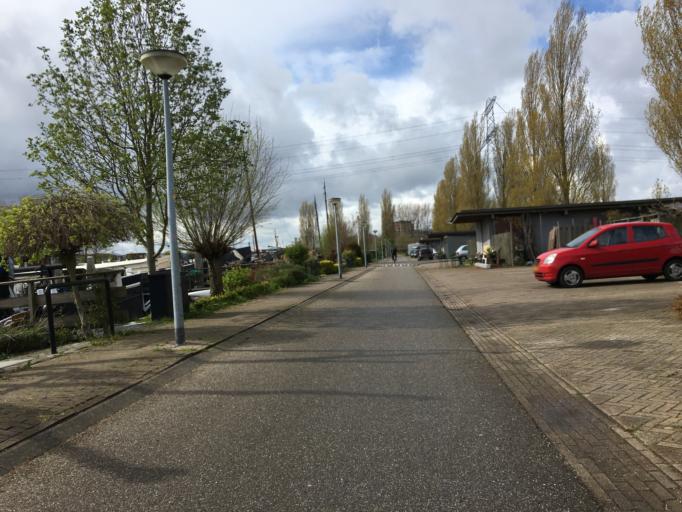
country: NL
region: Flevoland
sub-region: Gemeente Almere
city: Almere Stad
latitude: 52.3719
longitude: 5.2582
